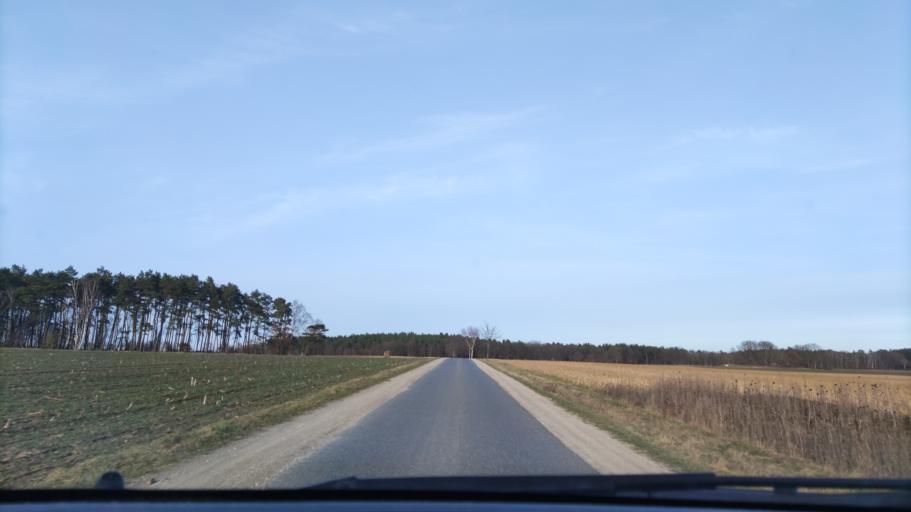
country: DE
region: Lower Saxony
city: Dahlenburg
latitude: 53.1993
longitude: 10.7006
